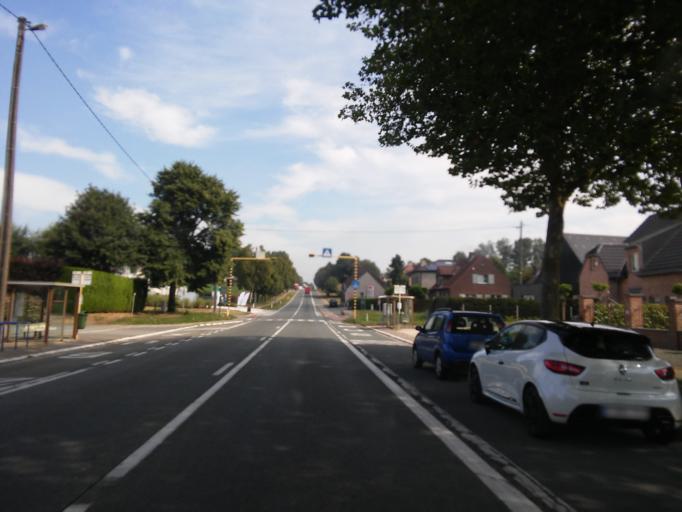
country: BE
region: Flanders
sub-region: Provincie Vlaams-Brabant
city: Gooik
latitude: 50.7908
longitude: 4.1246
